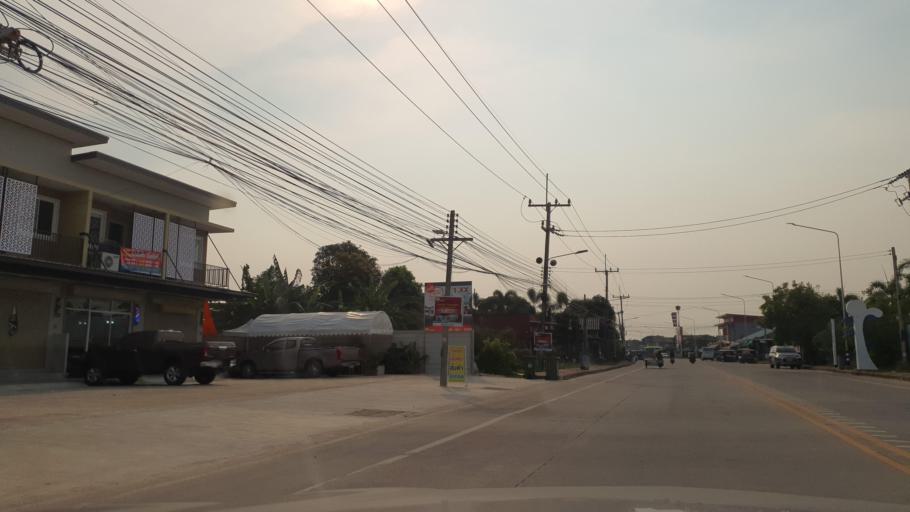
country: TH
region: Rayong
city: Rayong
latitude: 12.6172
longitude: 101.4131
